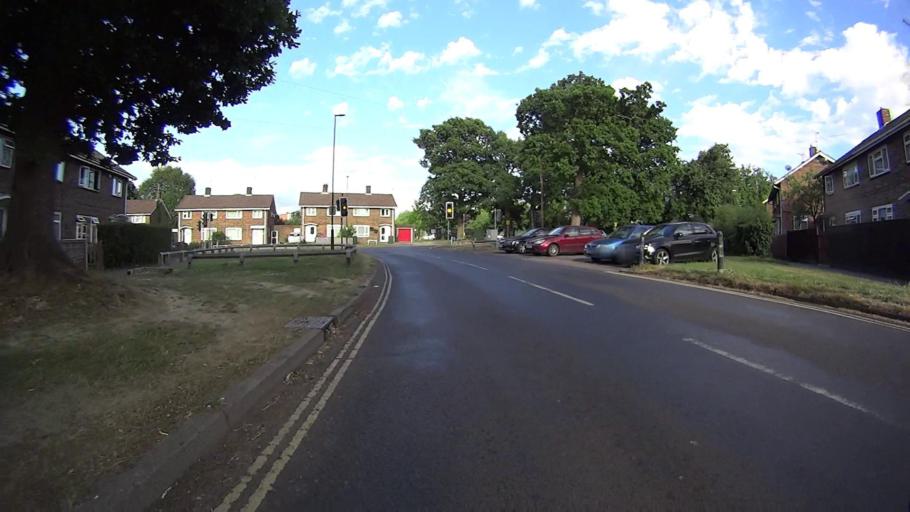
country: GB
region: England
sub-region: West Sussex
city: Gossops Green
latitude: 51.1166
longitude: -0.2159
